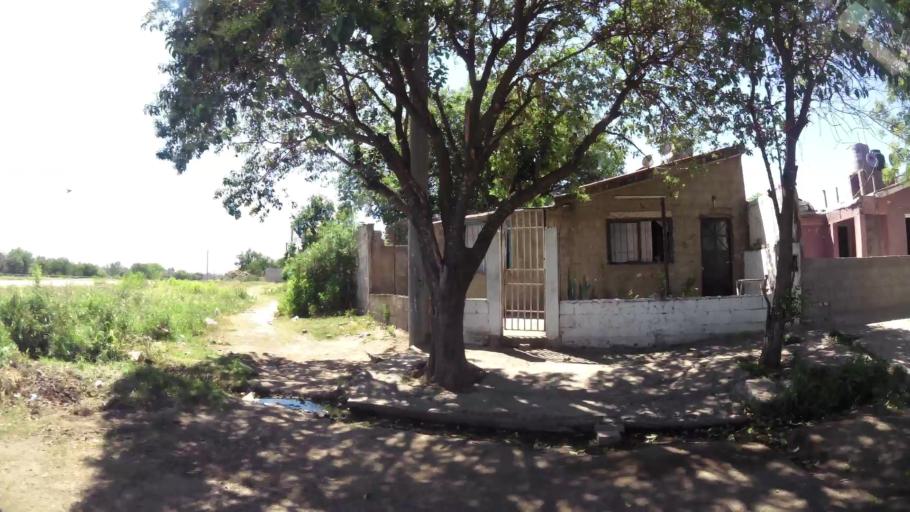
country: AR
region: Cordoba
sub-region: Departamento de Capital
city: Cordoba
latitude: -31.4074
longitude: -64.1385
